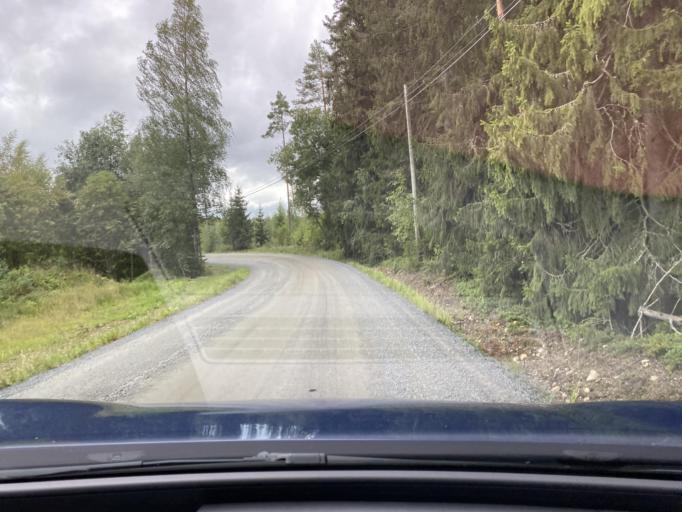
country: FI
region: Pirkanmaa
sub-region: Lounais-Pirkanmaa
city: Vammala
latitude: 61.2702
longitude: 22.9653
